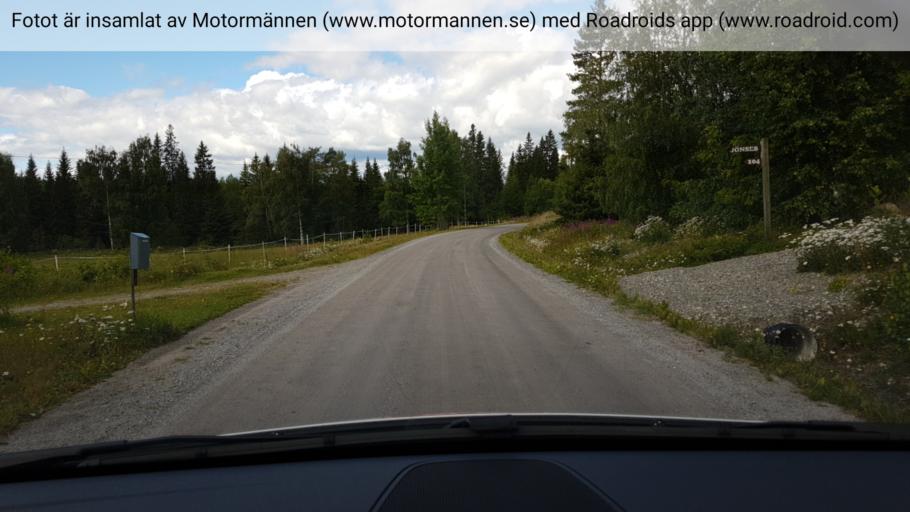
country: SE
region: Jaemtland
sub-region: Braecke Kommun
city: Braecke
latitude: 63.1020
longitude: 15.7523
